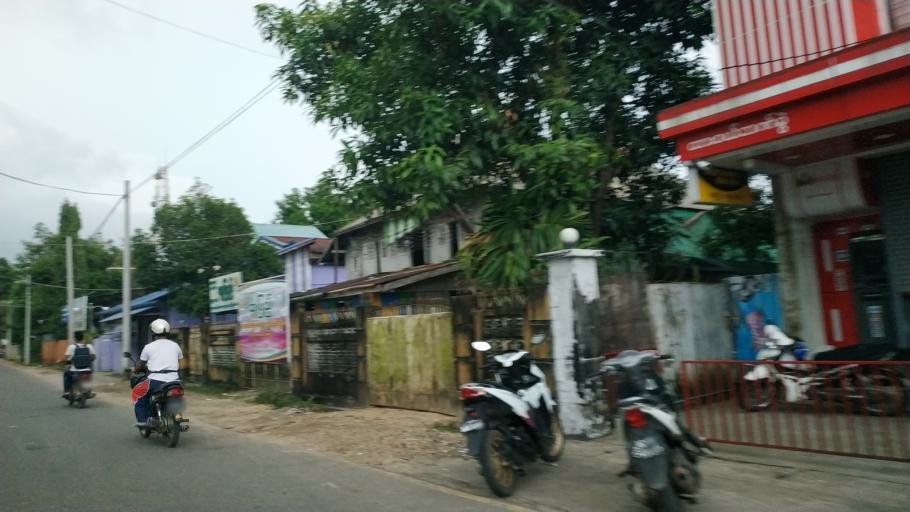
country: MM
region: Tanintharyi
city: Dawei
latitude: 14.0708
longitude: 98.1942
